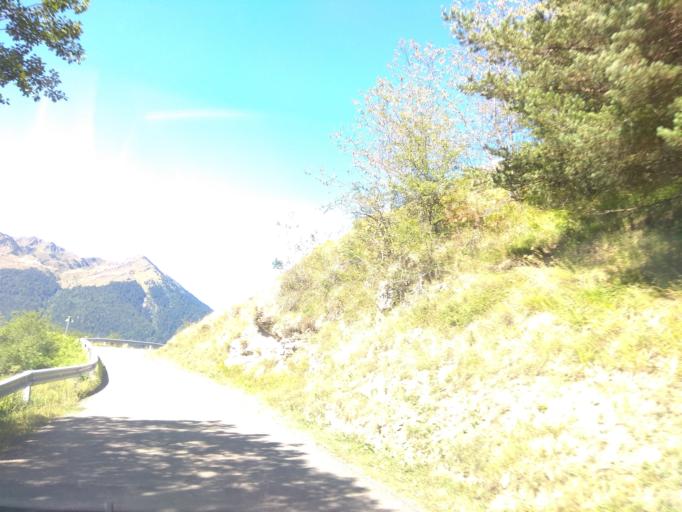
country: ES
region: Catalonia
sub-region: Provincia de Lleida
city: Les
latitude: 42.7517
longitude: 0.7164
